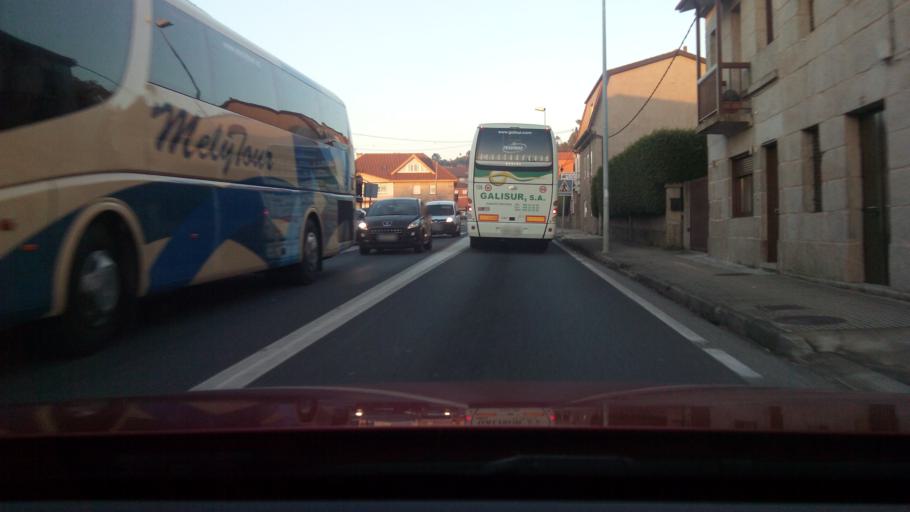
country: ES
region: Galicia
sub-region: Provincia de Pontevedra
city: Gondomar
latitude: 42.1437
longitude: -8.7301
